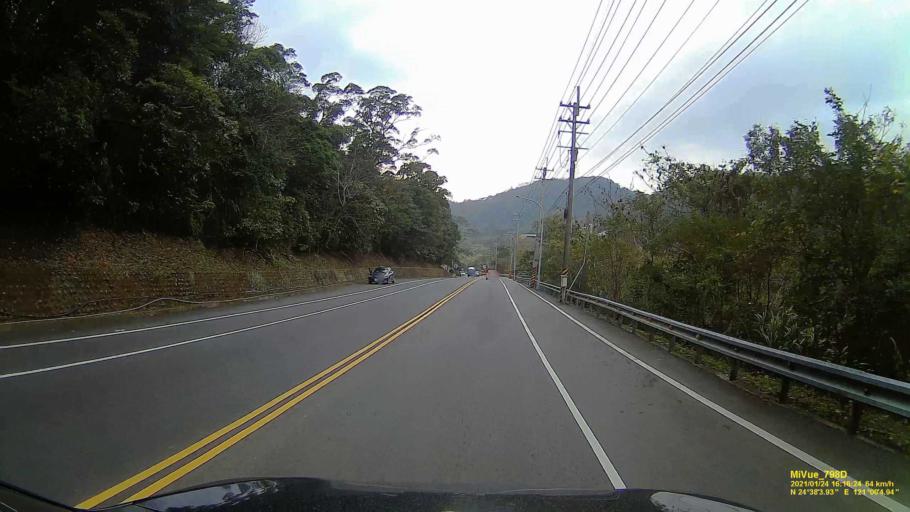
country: TW
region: Taiwan
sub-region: Hsinchu
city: Hsinchu
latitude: 24.6346
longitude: 121.0010
